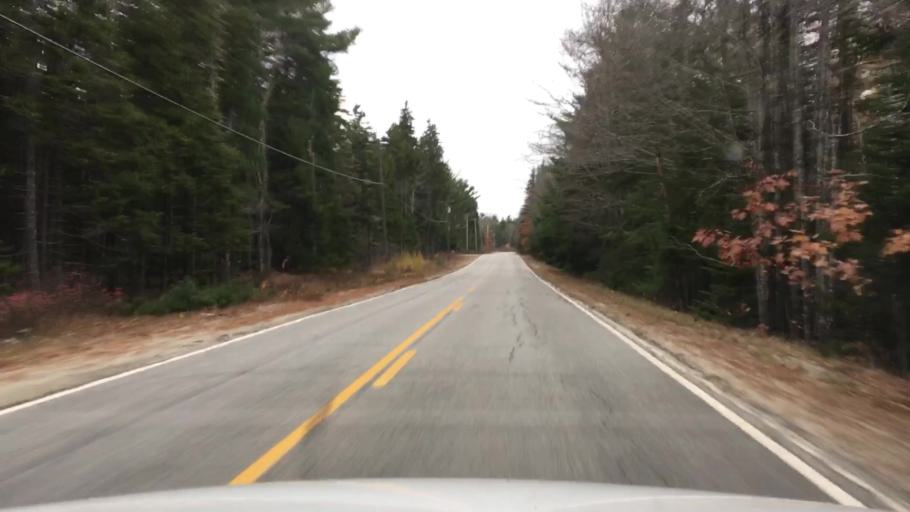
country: US
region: Maine
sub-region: Hancock County
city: Sedgwick
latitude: 44.2846
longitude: -68.5547
